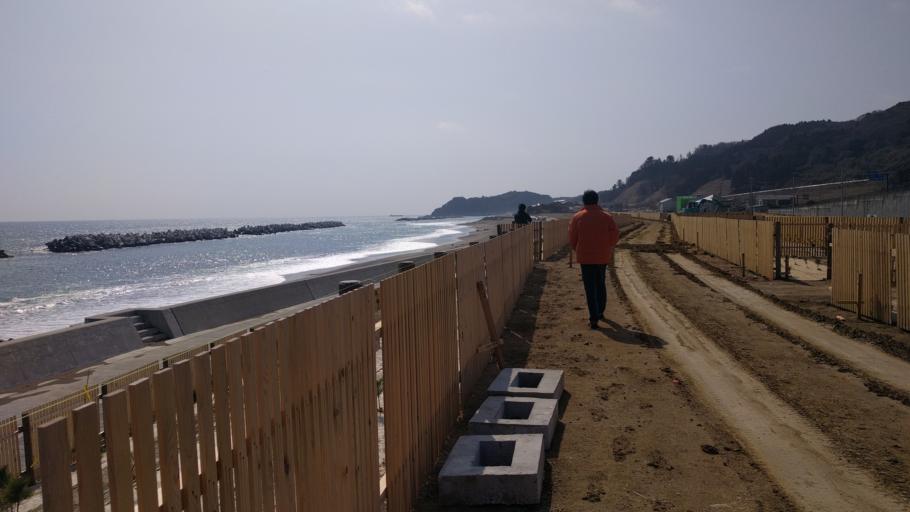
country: JP
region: Fukushima
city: Iwaki
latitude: 37.1379
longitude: 140.9984
